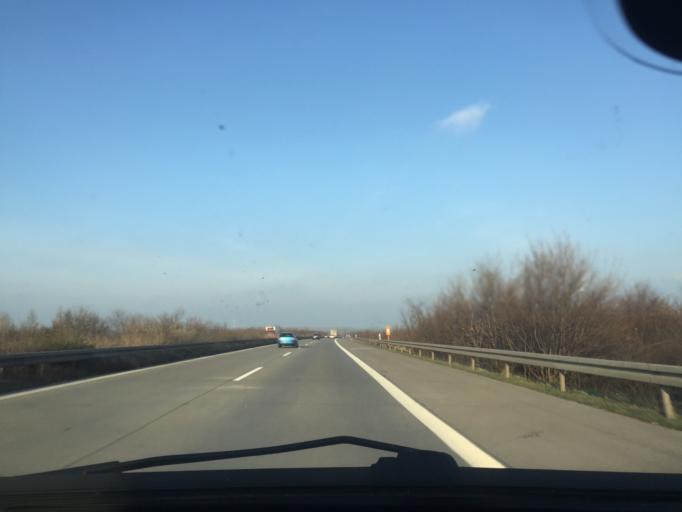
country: DE
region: Saxony-Anhalt
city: Hohendodeleben
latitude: 52.1038
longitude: 11.5286
